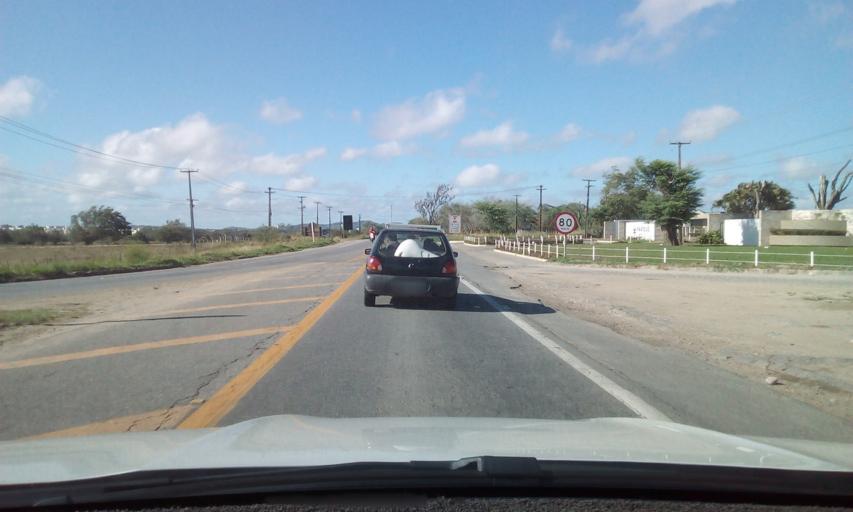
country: BR
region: Paraiba
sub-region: Campina Grande
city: Campina Grande
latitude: -7.2792
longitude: -35.8890
